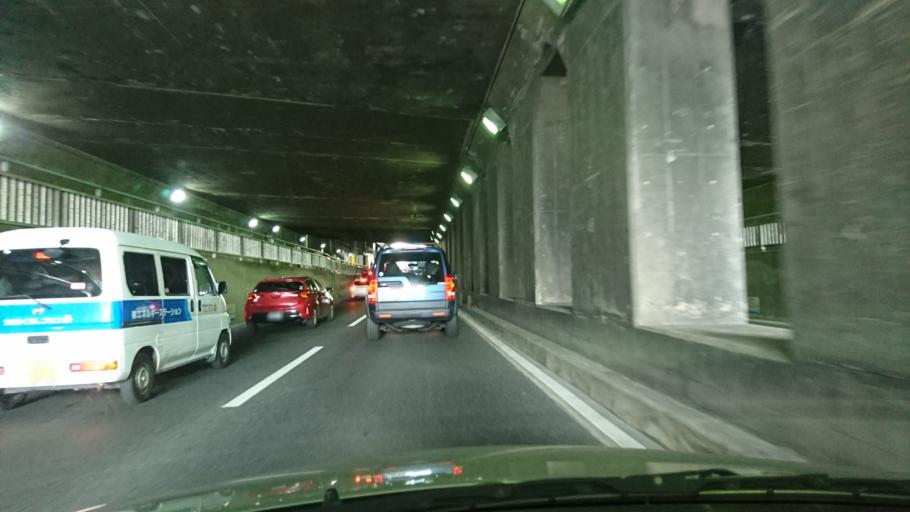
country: JP
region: Hyogo
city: Akashi
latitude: 34.6669
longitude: 134.9598
